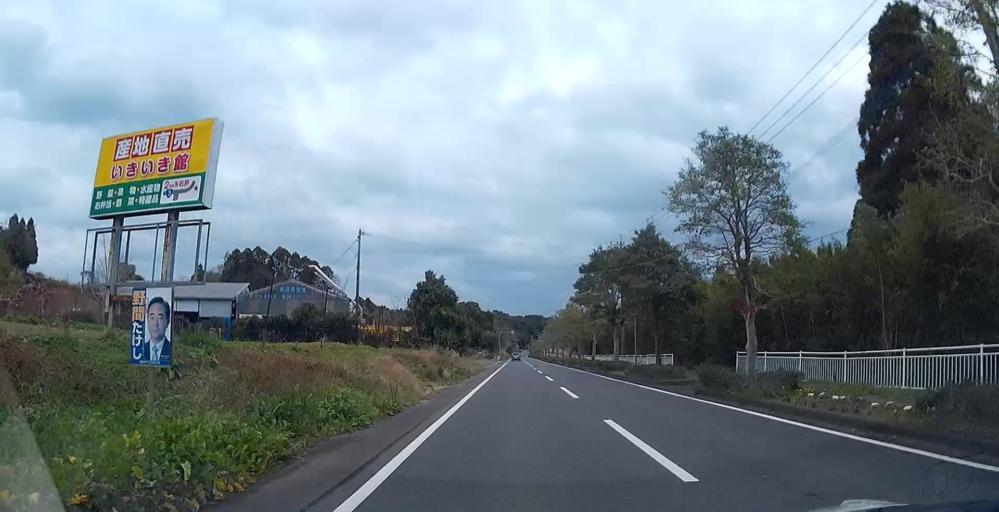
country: JP
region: Kagoshima
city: Akune
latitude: 32.0727
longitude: 130.2148
